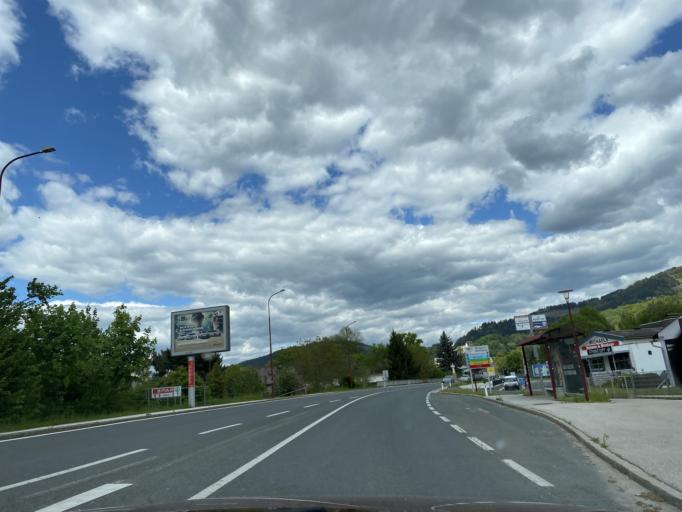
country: AT
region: Carinthia
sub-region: Politischer Bezirk Wolfsberg
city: Wolfsberg
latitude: 46.8290
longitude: 14.8396
